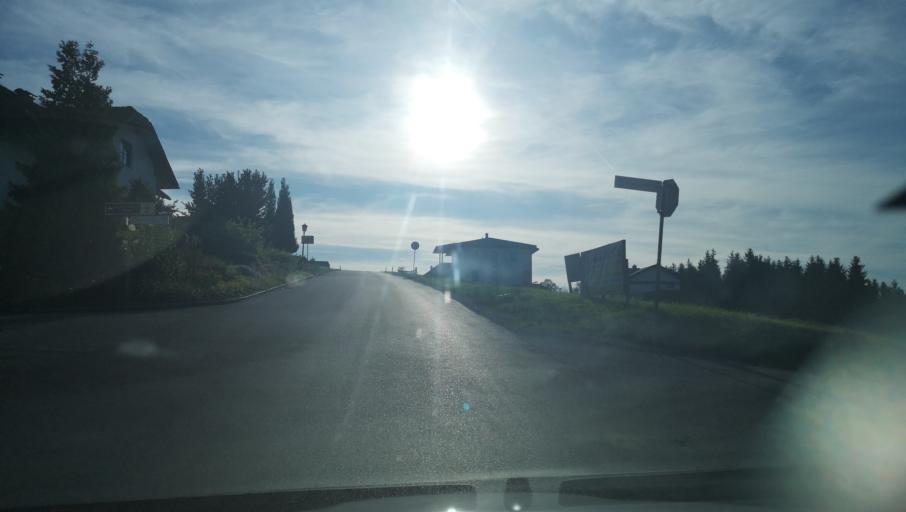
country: AT
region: Lower Austria
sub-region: Politischer Bezirk Amstetten
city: Ybbsitz
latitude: 47.9952
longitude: 14.8720
